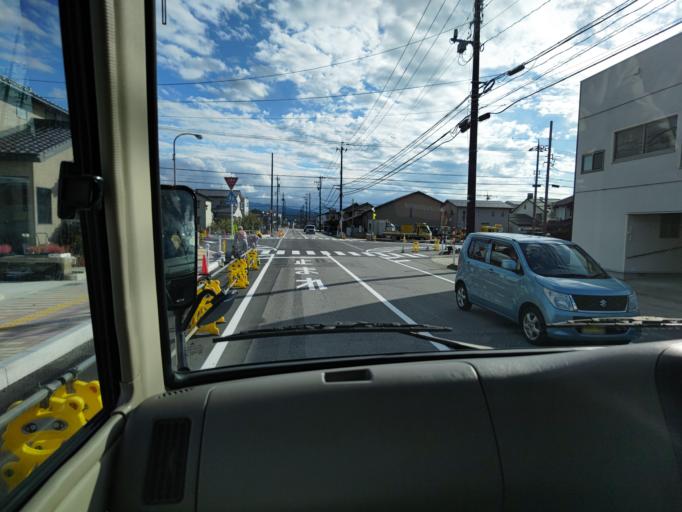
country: JP
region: Toyama
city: Nyuzen
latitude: 36.8768
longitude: 137.4467
